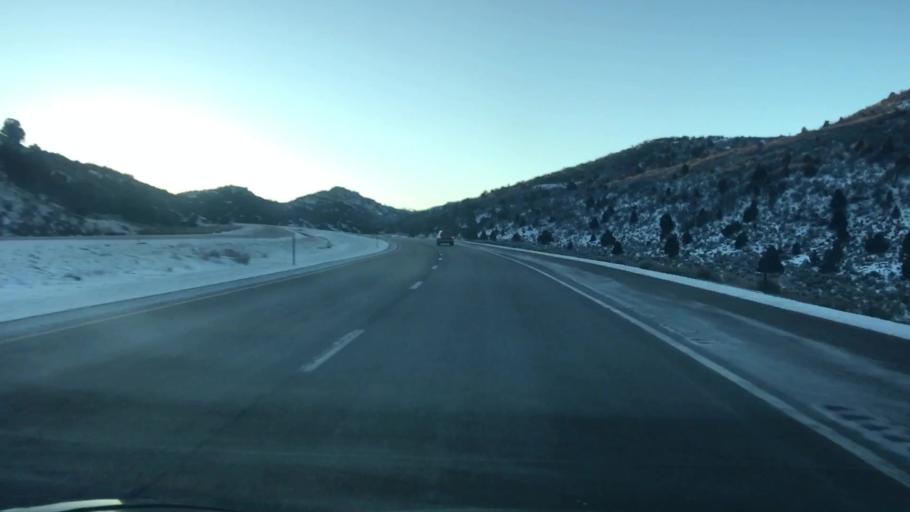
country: US
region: Utah
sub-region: Sevier County
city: Salina
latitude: 38.7899
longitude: -111.5043
